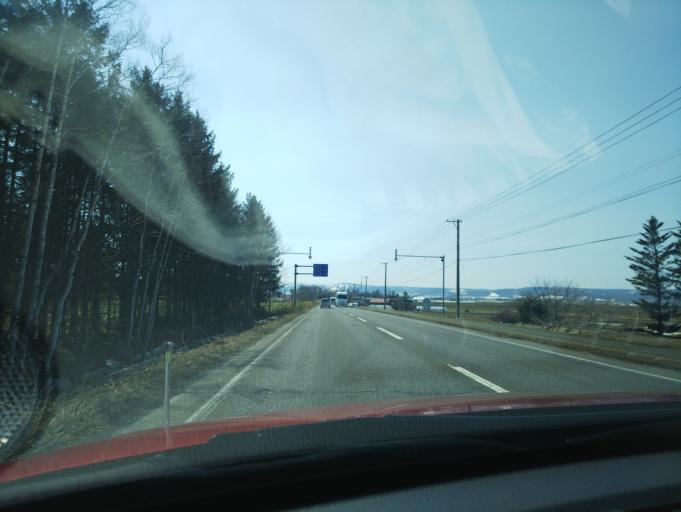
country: JP
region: Hokkaido
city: Nayoro
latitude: 44.3080
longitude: 142.4422
